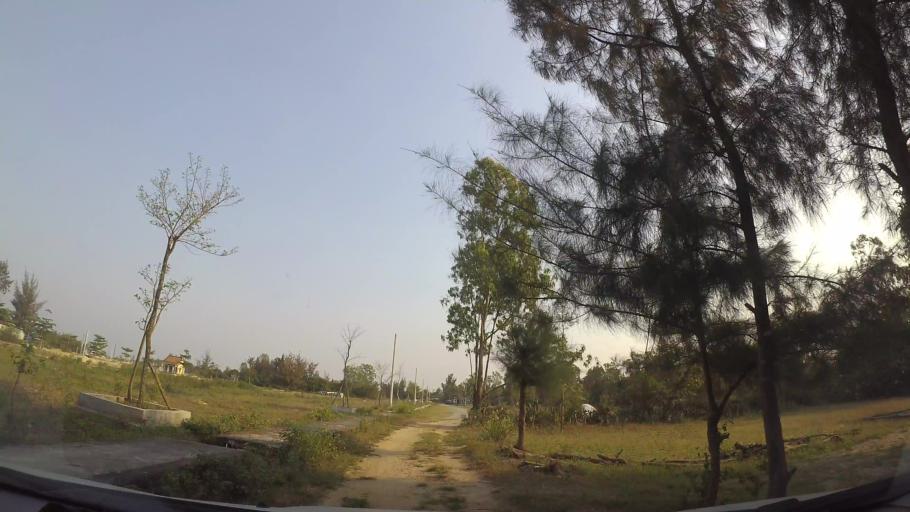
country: VN
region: Da Nang
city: Ngu Hanh Son
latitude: 15.9613
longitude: 108.2651
